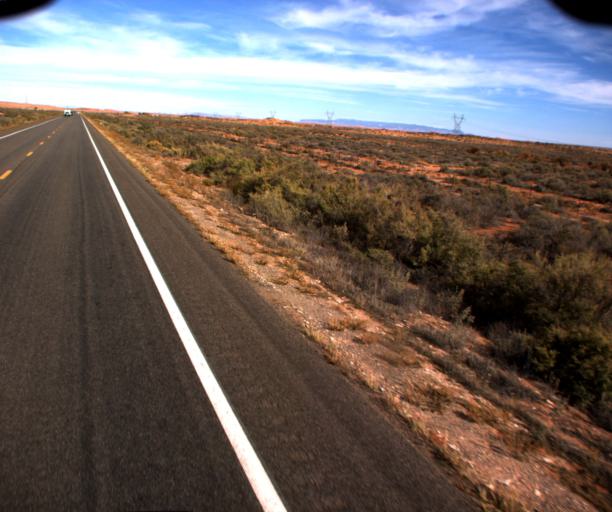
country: US
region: Arizona
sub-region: Navajo County
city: Kayenta
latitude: 36.8063
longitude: -109.9111
